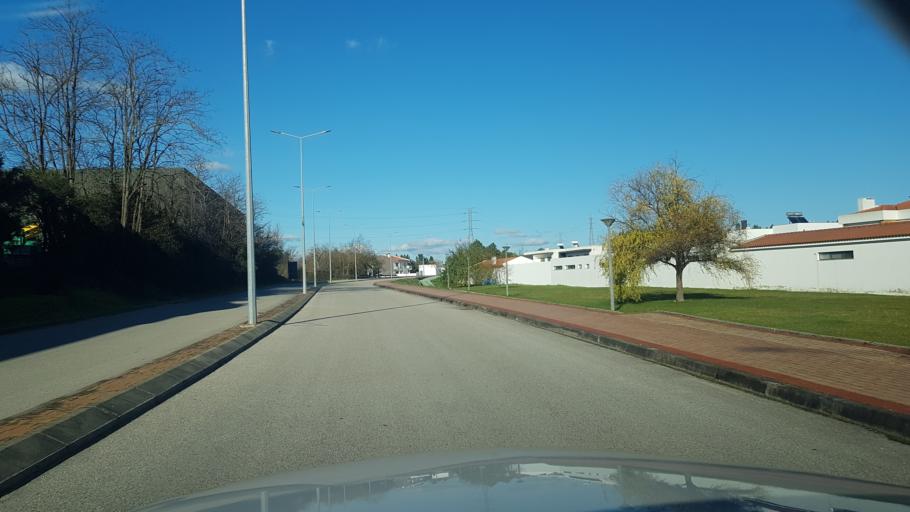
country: PT
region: Santarem
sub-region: Entroncamento
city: Entroncamento
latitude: 39.4820
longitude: -8.4719
